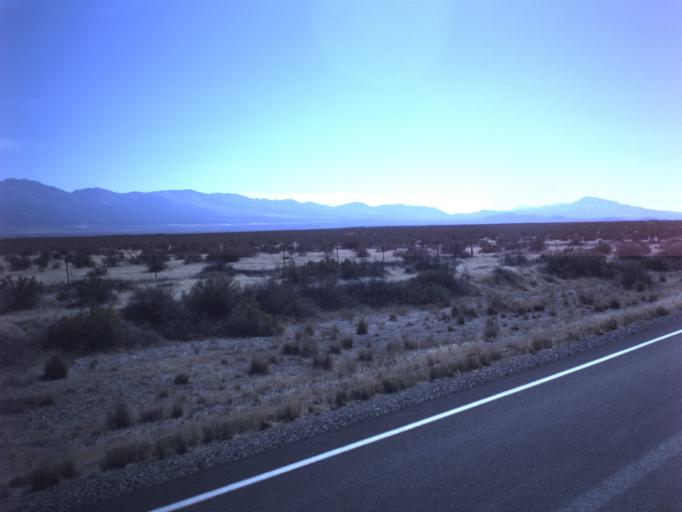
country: US
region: Utah
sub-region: Tooele County
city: Grantsville
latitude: 40.3325
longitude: -112.7444
